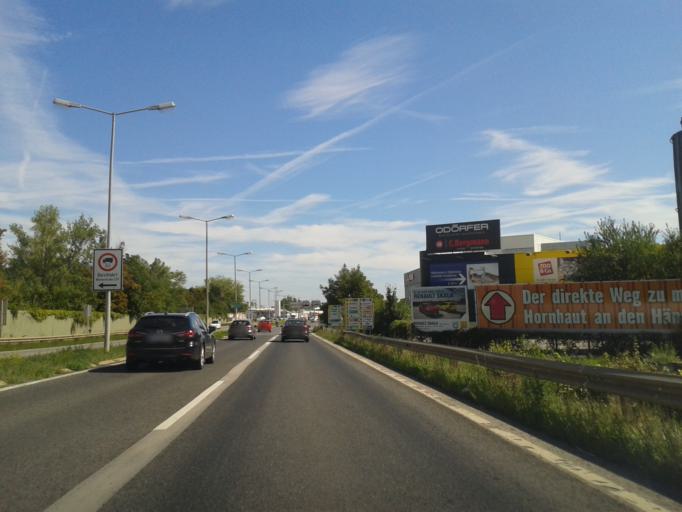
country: AT
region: Lower Austria
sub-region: Politischer Bezirk Modling
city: Brunn am Gebirge
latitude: 48.1146
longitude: 16.3016
